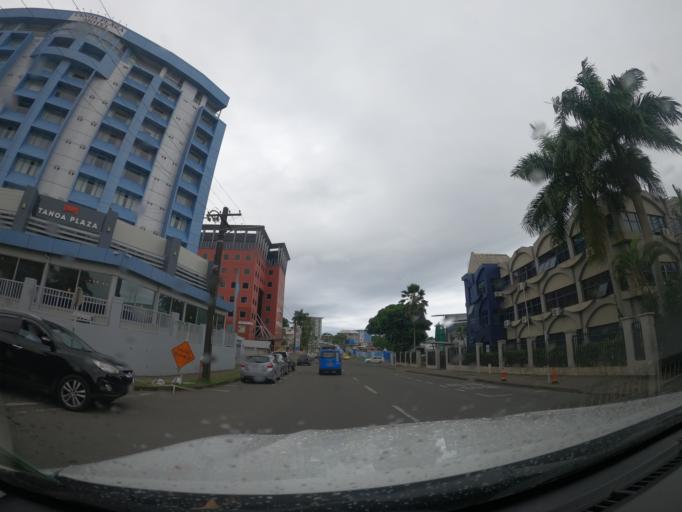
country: FJ
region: Central
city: Suva
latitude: -18.1437
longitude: 178.4261
